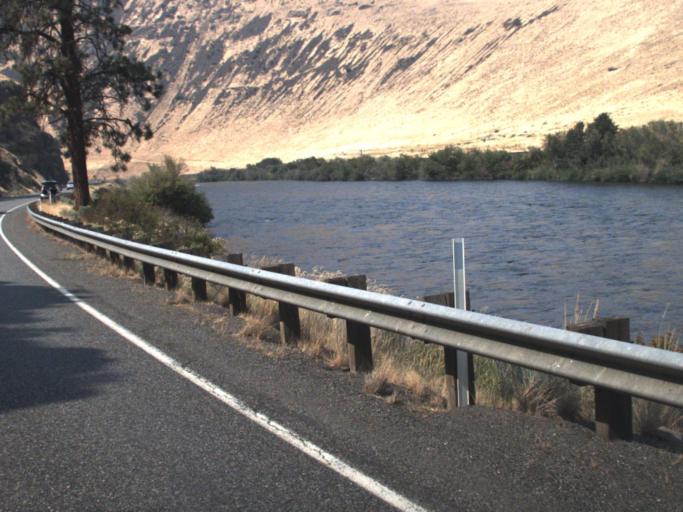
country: US
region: Washington
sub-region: Kittitas County
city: Kittitas
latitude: 46.8753
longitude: -120.4873
